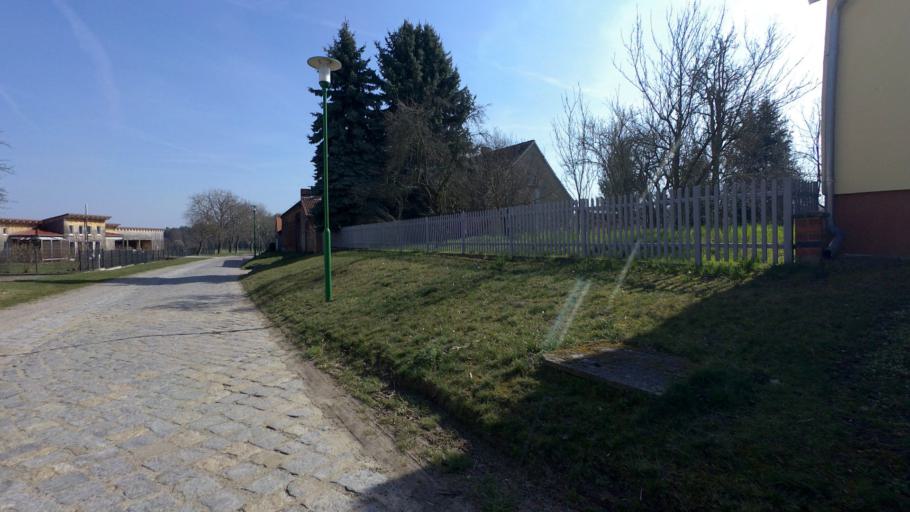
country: DE
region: Brandenburg
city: Golssen
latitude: 51.9831
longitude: 13.5445
